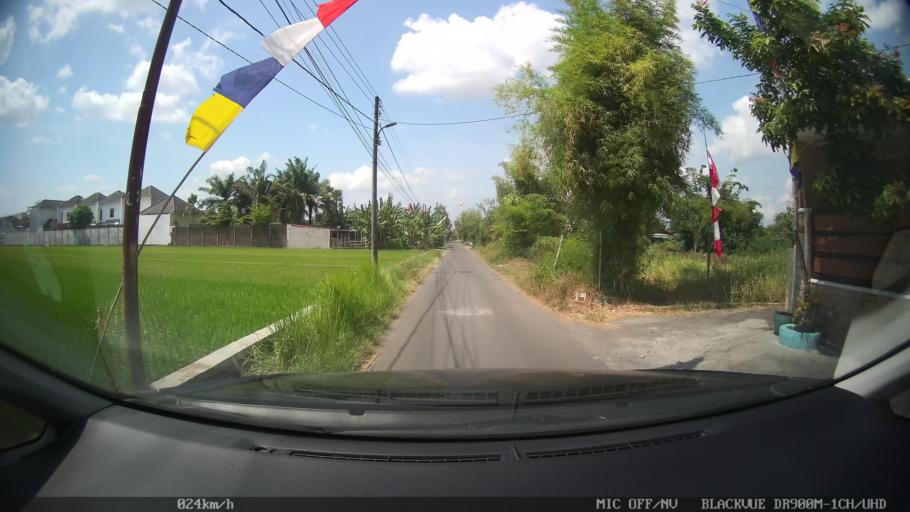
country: ID
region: Daerah Istimewa Yogyakarta
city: Sewon
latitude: -7.8312
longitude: 110.3781
